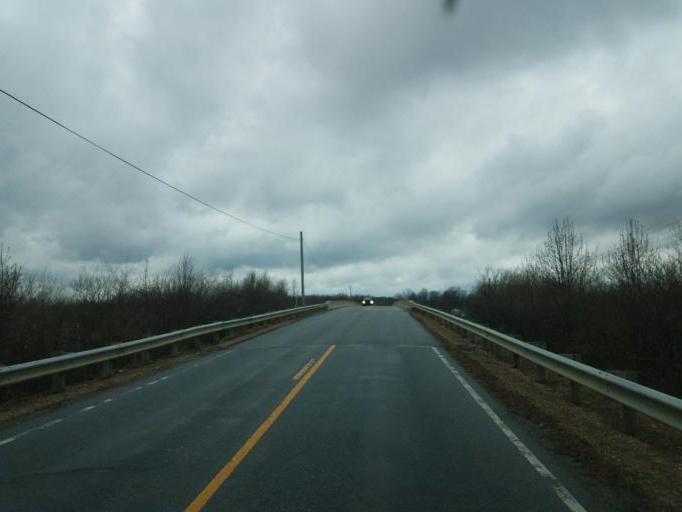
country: US
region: Ohio
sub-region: Delaware County
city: Sunbury
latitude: 40.2413
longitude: -82.9273
